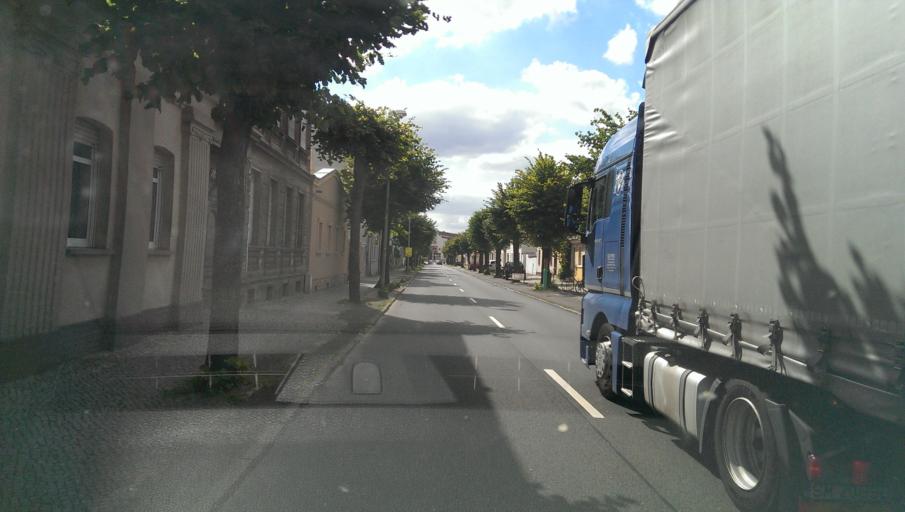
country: DE
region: Saxony-Anhalt
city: Coswig
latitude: 51.8858
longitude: 12.4554
